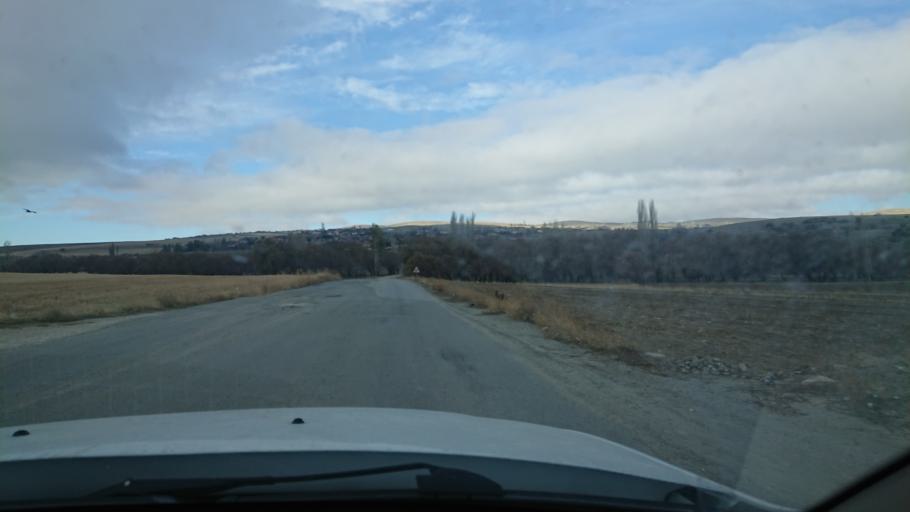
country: TR
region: Aksaray
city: Ortakoy
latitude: 38.7525
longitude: 34.0220
